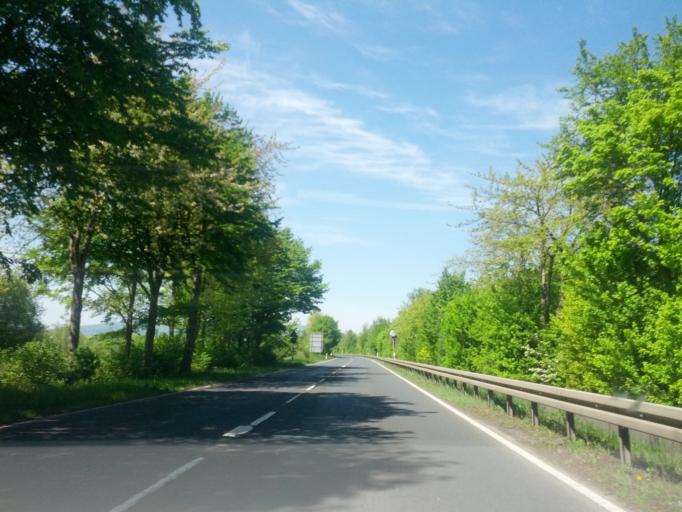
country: DE
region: Hesse
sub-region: Regierungsbezirk Kassel
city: Eschwege
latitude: 51.1970
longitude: 10.0749
